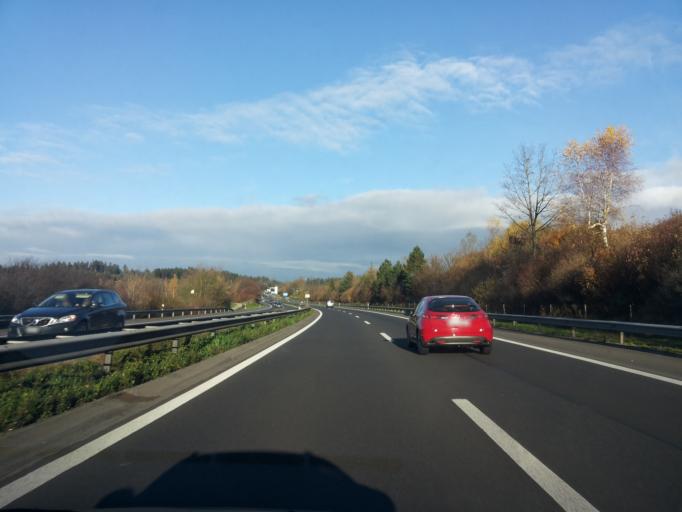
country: CH
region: Lucerne
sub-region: Sursee District
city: Neuenkirch
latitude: 47.1059
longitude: 8.2424
